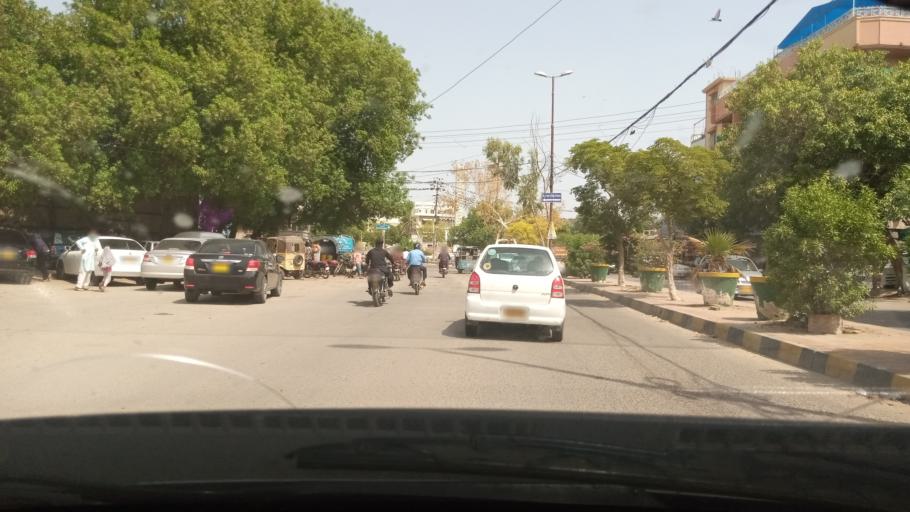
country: PK
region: Sindh
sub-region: Karachi District
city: Karachi
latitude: 24.8735
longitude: 67.0478
